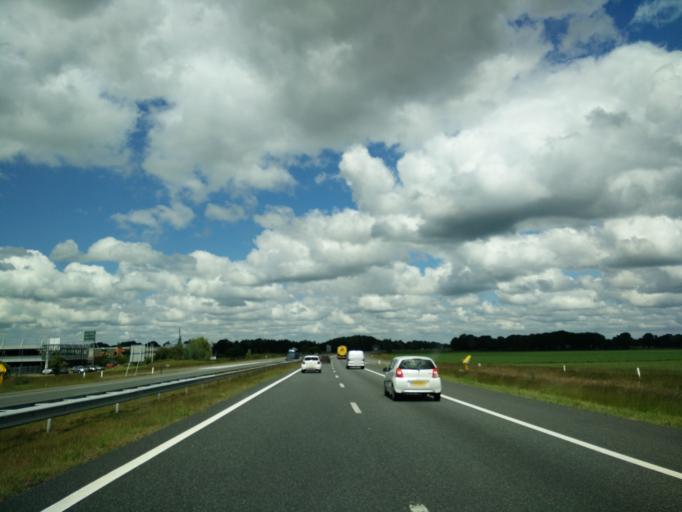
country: NL
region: Drenthe
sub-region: Gemeente Tynaarlo
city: Tynaarlo
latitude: 53.0829
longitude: 6.6039
